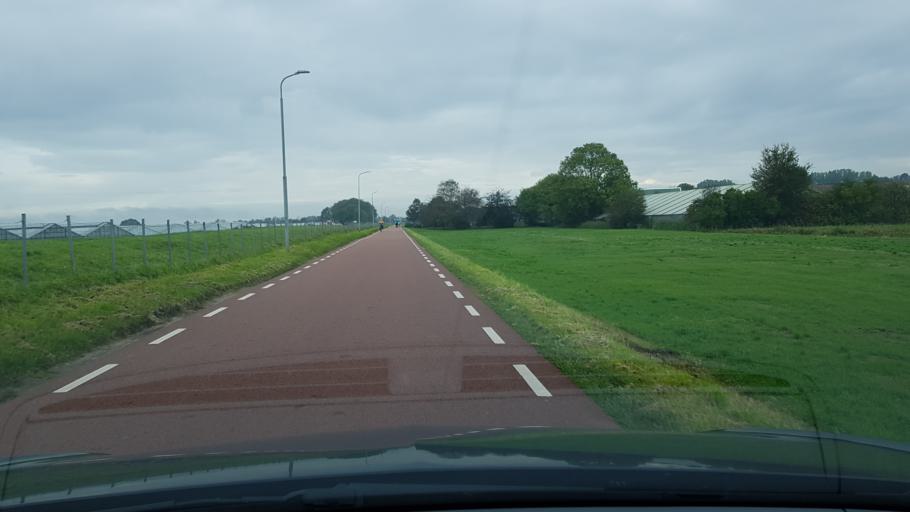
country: NL
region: North Holland
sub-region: Gemeente Aalsmeer
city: Aalsmeer
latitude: 52.2461
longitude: 4.7813
